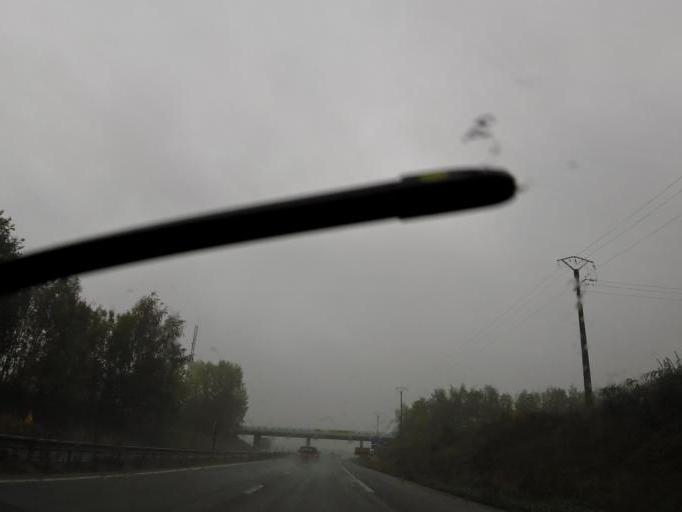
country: FR
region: Picardie
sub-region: Departement de l'Aisne
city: Montreuil-aux-Lions
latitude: 49.0169
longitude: 3.1569
